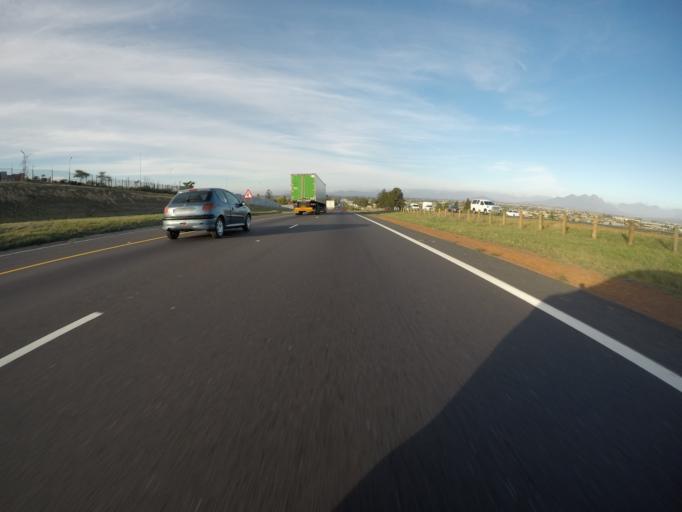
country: ZA
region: Western Cape
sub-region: City of Cape Town
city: Kraaifontein
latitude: -33.8564
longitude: 18.6977
